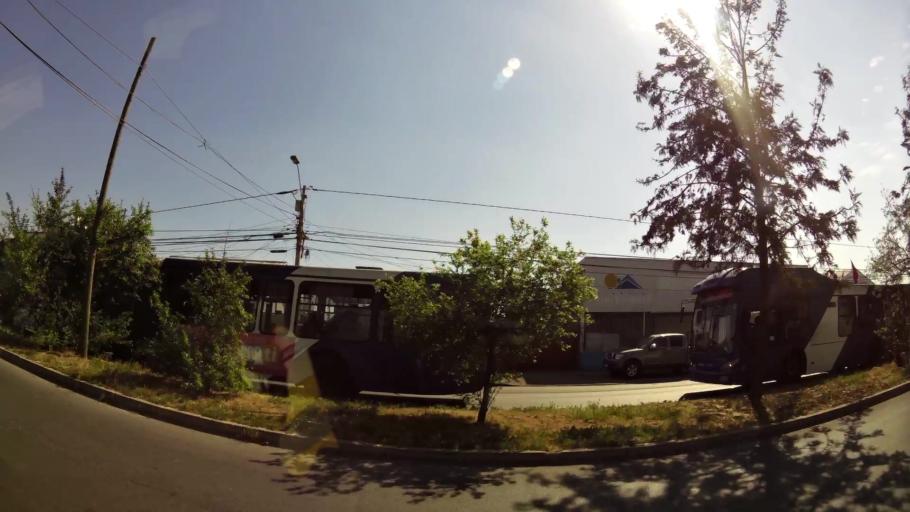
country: CL
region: Santiago Metropolitan
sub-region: Provincia de Santiago
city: La Pintana
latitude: -33.5276
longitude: -70.6098
